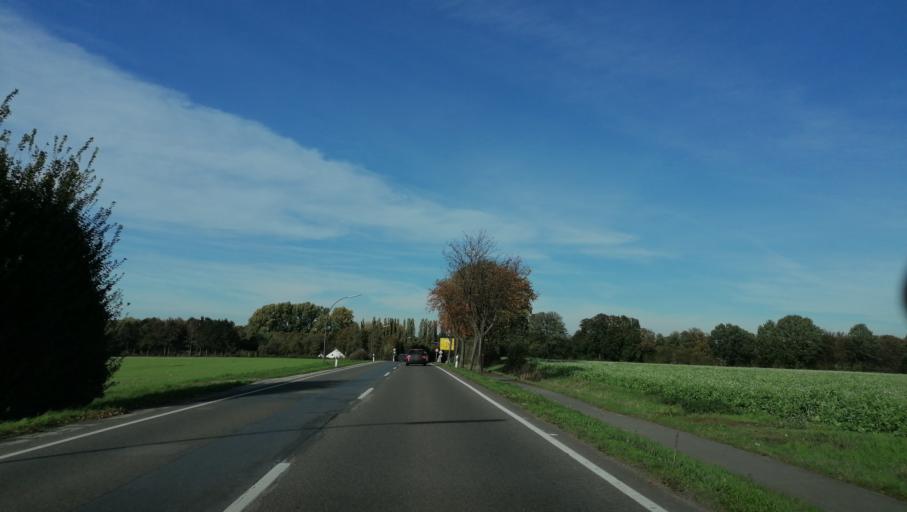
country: DE
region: North Rhine-Westphalia
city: Herten
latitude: 51.6238
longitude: 7.1593
